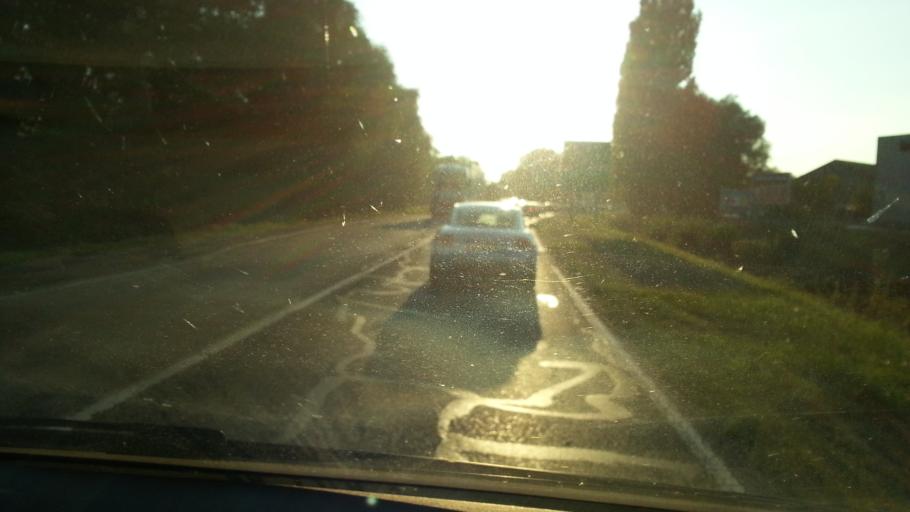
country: FR
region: Picardie
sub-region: Departement de l'Oise
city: Villers-Saint-Paul
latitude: 49.2849
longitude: 2.4931
